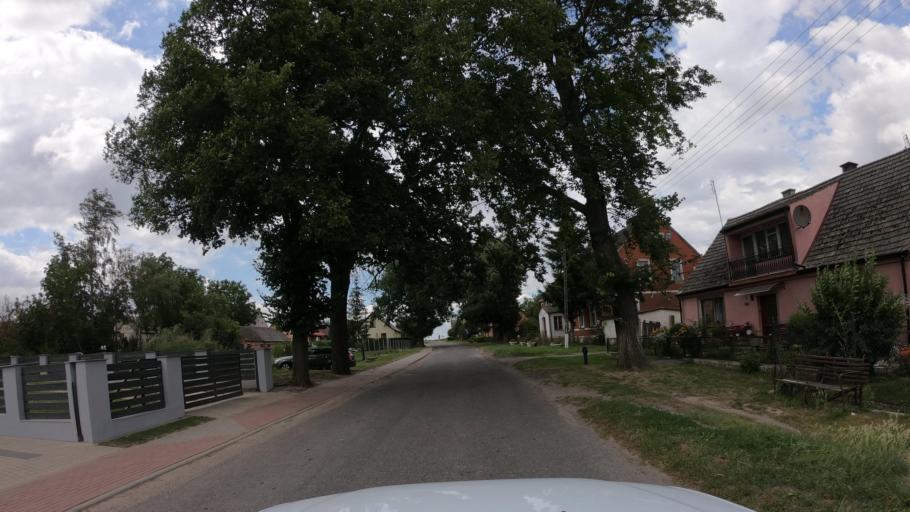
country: PL
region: West Pomeranian Voivodeship
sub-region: Powiat pyrzycki
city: Warnice
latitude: 53.2019
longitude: 14.9882
